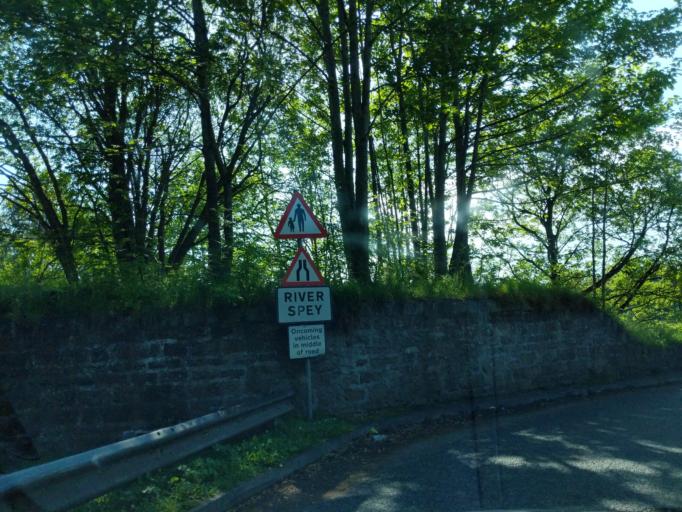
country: GB
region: Scotland
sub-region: Moray
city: Rothes
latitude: 57.5504
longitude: -3.1398
